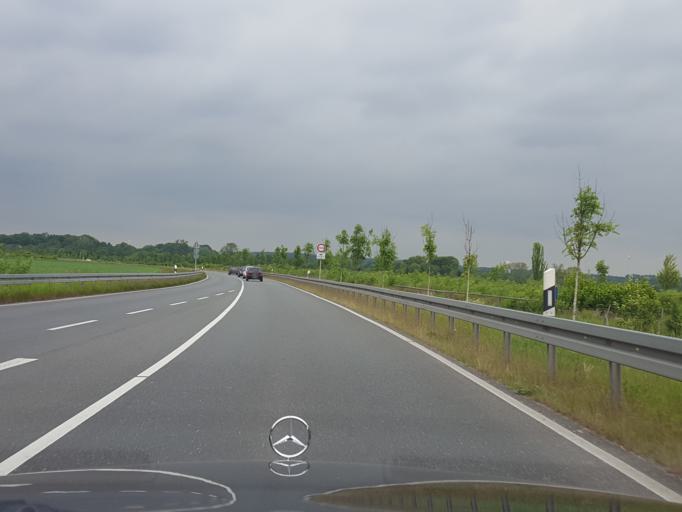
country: DE
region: North Rhine-Westphalia
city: Oer-Erkenschwick
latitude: 51.6340
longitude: 7.3004
